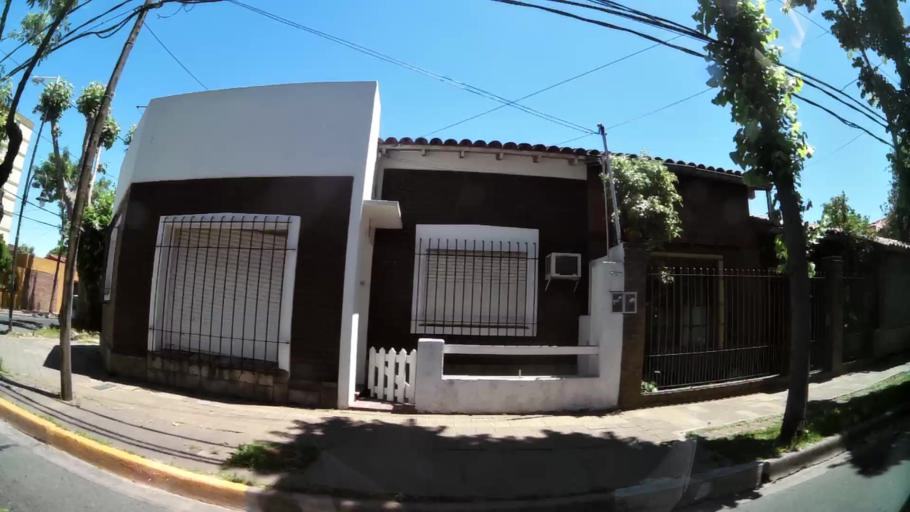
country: AR
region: Buenos Aires
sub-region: Partido de Tigre
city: Tigre
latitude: -34.4492
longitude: -58.5491
